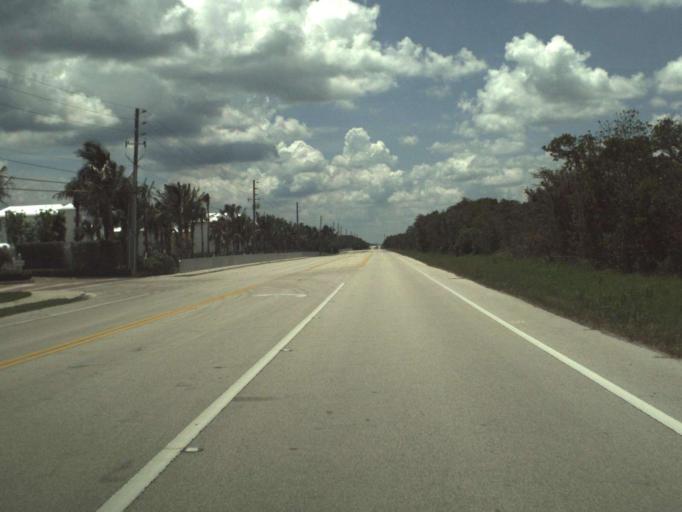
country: US
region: Florida
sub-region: Saint Lucie County
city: Indian River Estates
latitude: 27.3914
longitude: -80.2616
